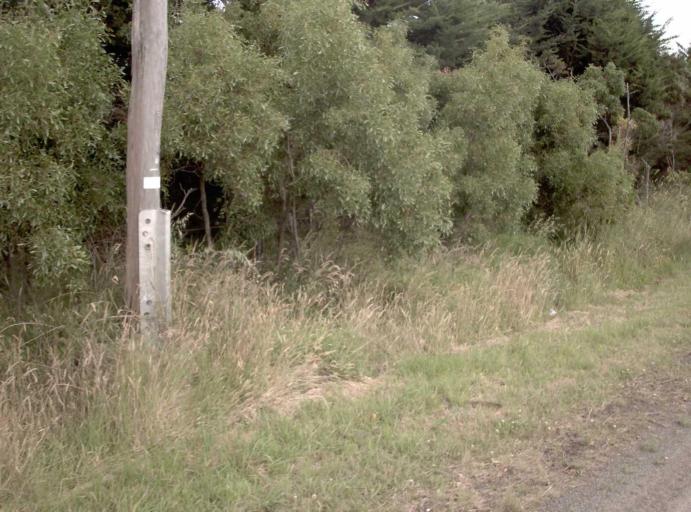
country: AU
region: Victoria
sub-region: Latrobe
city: Morwell
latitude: -38.2129
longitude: 146.4452
